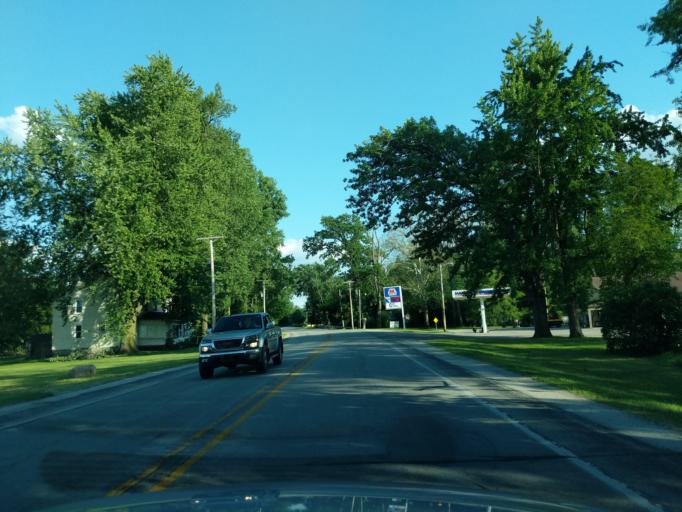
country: US
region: Indiana
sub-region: Whitley County
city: Tri-Lakes
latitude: 41.2752
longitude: -85.4921
